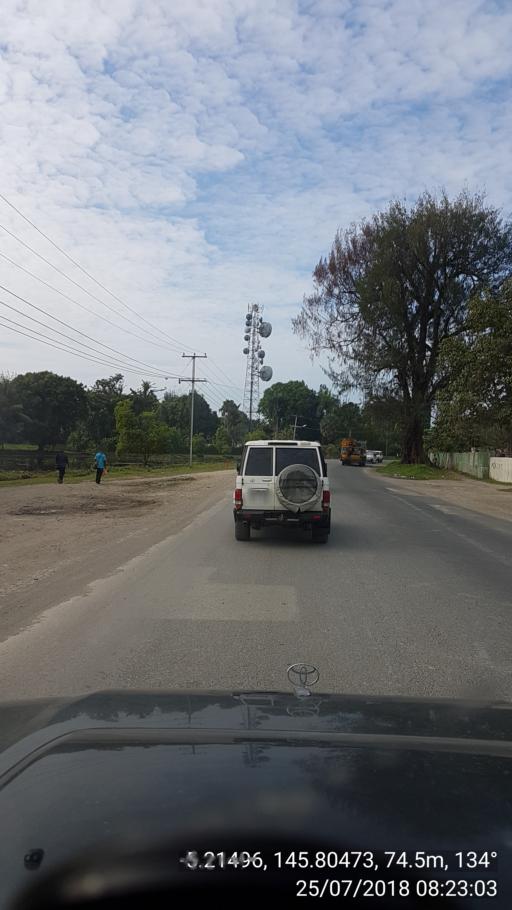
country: PG
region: Madang
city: Madang
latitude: -5.2150
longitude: 145.8047
